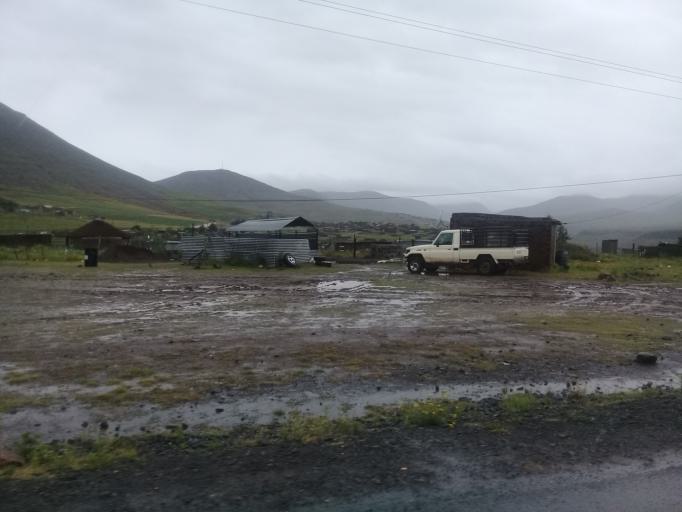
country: LS
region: Mokhotlong
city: Mokhotlong
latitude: -29.3344
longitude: 29.0329
